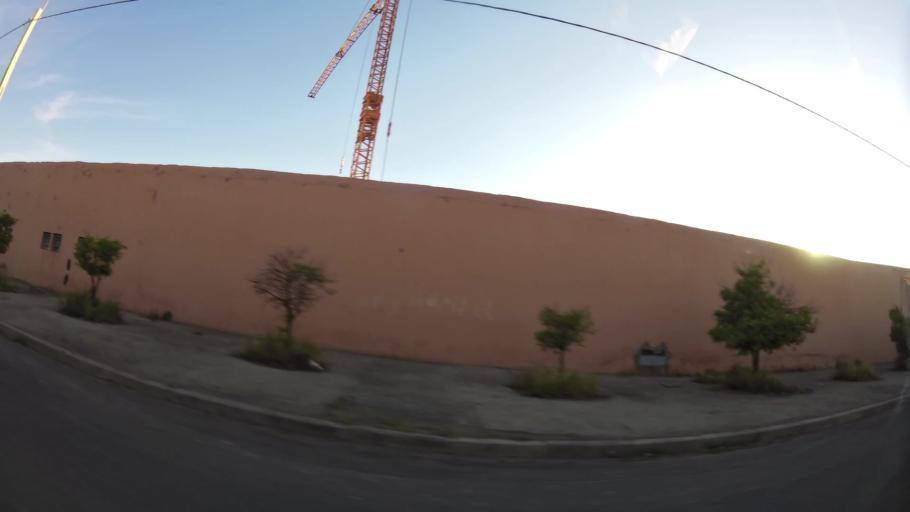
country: MA
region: Marrakech-Tensift-Al Haouz
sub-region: Marrakech
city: Marrakesh
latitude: 31.6676
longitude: -8.0375
